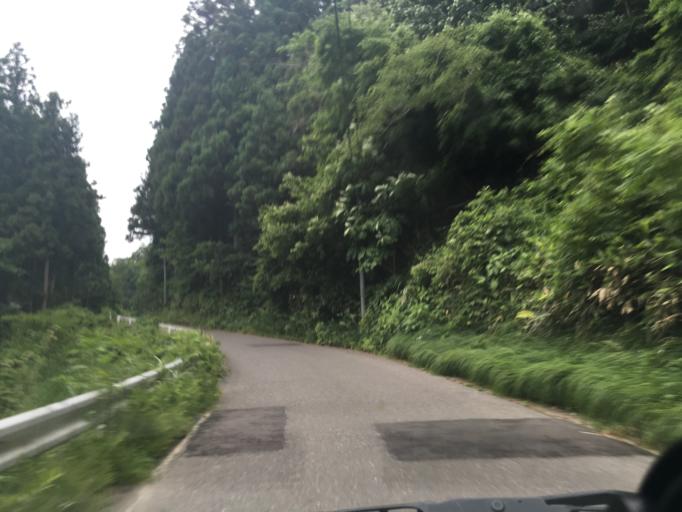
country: JP
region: Fukushima
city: Kitakata
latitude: 37.5219
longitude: 139.7283
